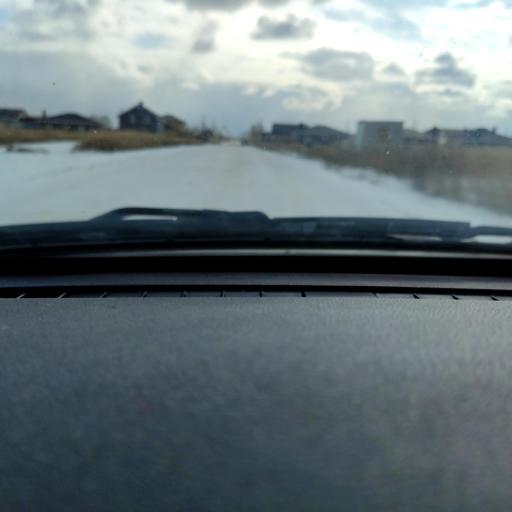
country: RU
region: Voronezj
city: Novaya Usman'
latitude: 51.6598
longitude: 39.4560
